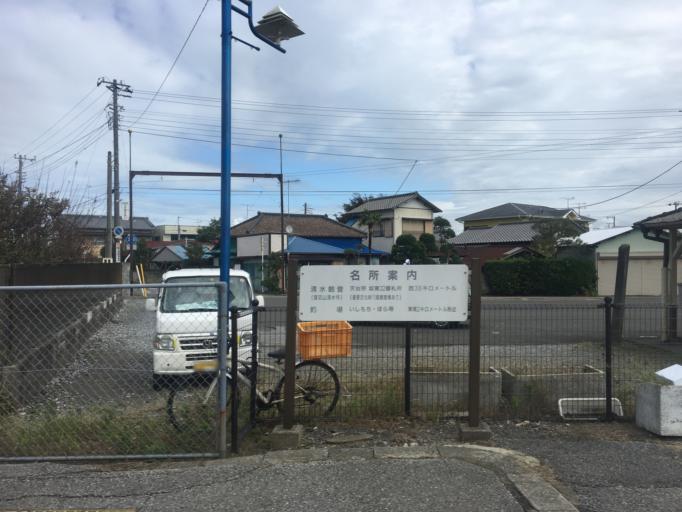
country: JP
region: Chiba
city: Ohara
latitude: 35.2960
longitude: 140.3849
